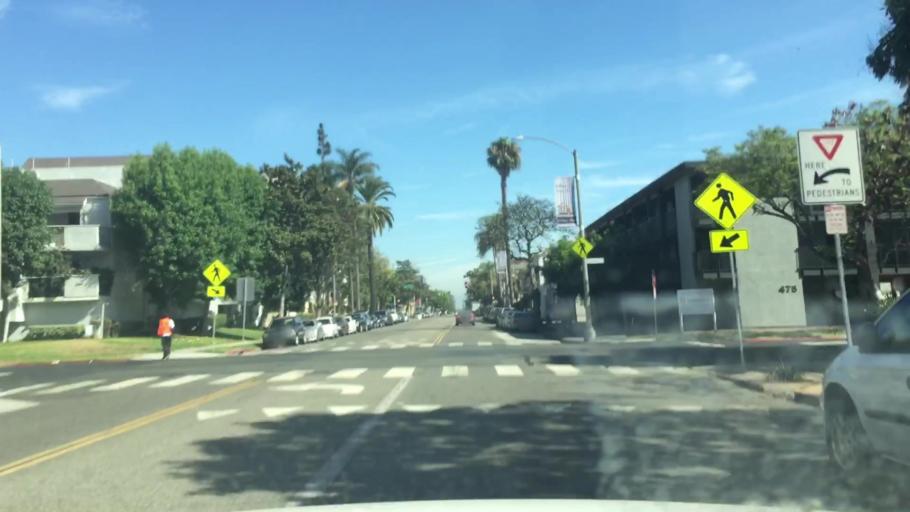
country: US
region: California
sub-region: Los Angeles County
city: Long Beach
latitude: 33.7726
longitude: -118.1980
